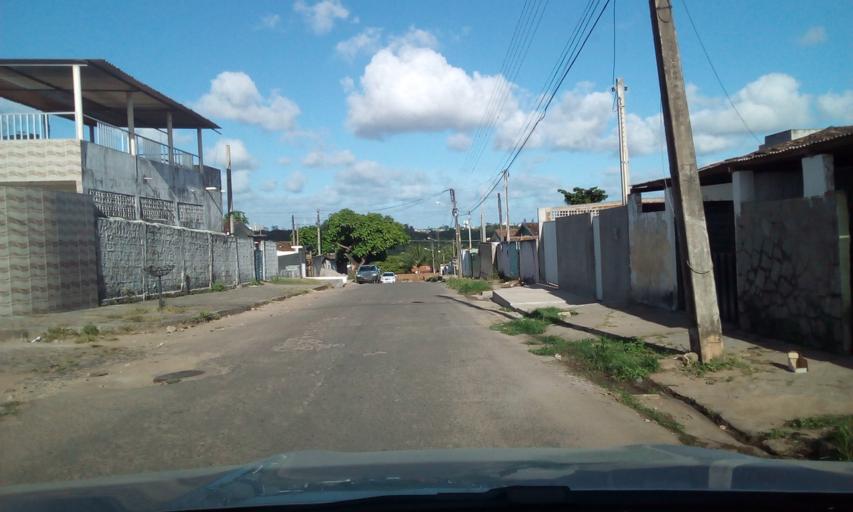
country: BR
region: Paraiba
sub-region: Bayeux
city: Bayeux
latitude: -7.1374
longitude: -34.9113
